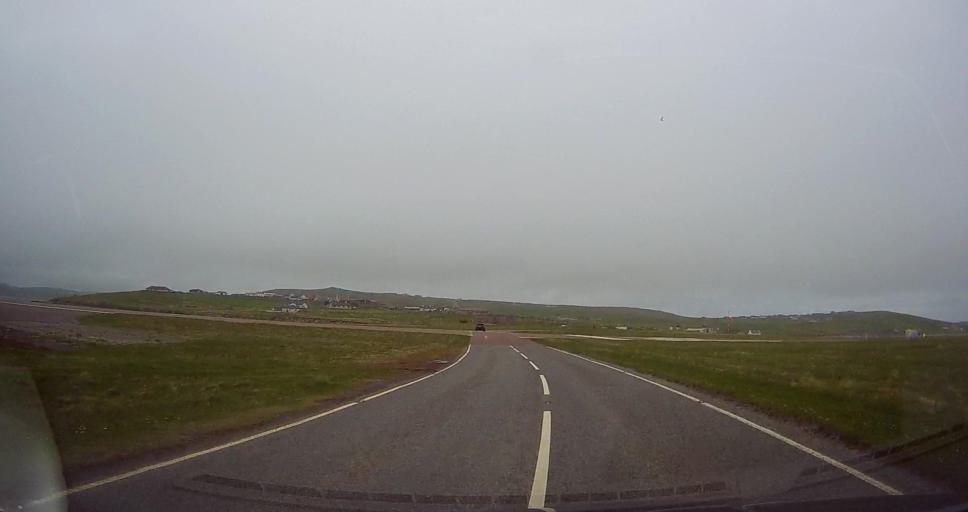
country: GB
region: Scotland
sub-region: Shetland Islands
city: Sandwick
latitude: 59.8798
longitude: -1.3059
